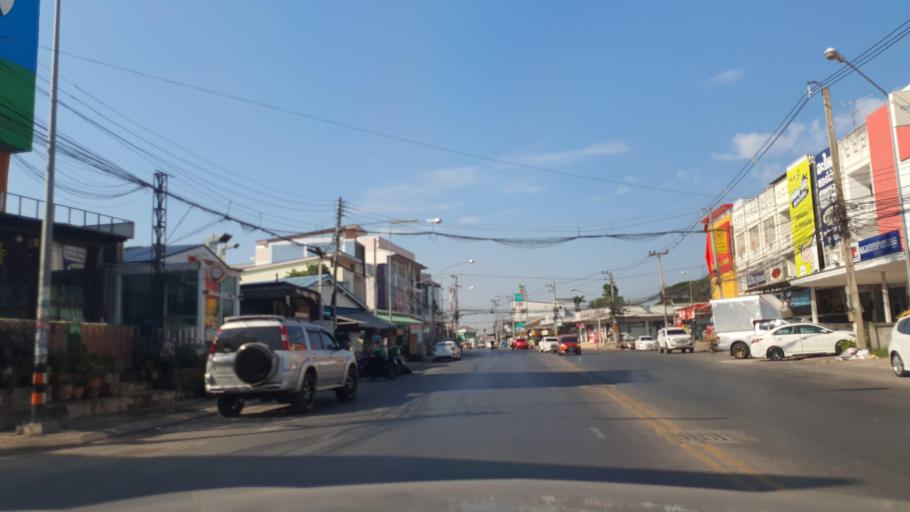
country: TH
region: Khon Kaen
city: Khon Kaen
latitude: 16.4344
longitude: 102.8155
